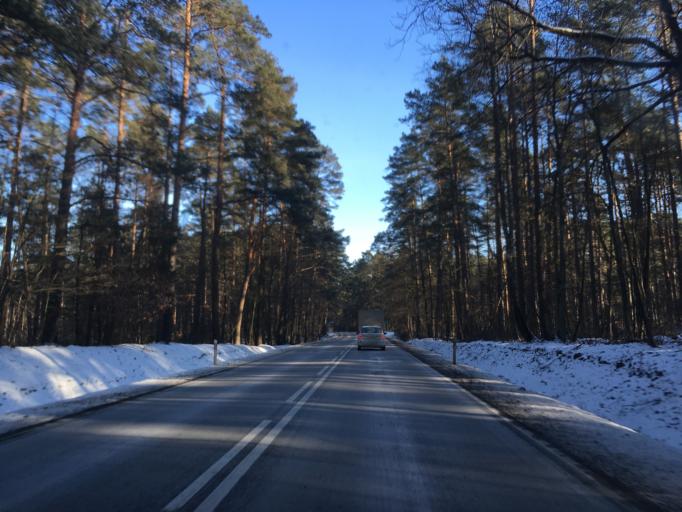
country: PL
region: Pomeranian Voivodeship
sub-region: Powiat koscierski
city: Koscierzyna
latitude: 54.1153
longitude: 17.8985
